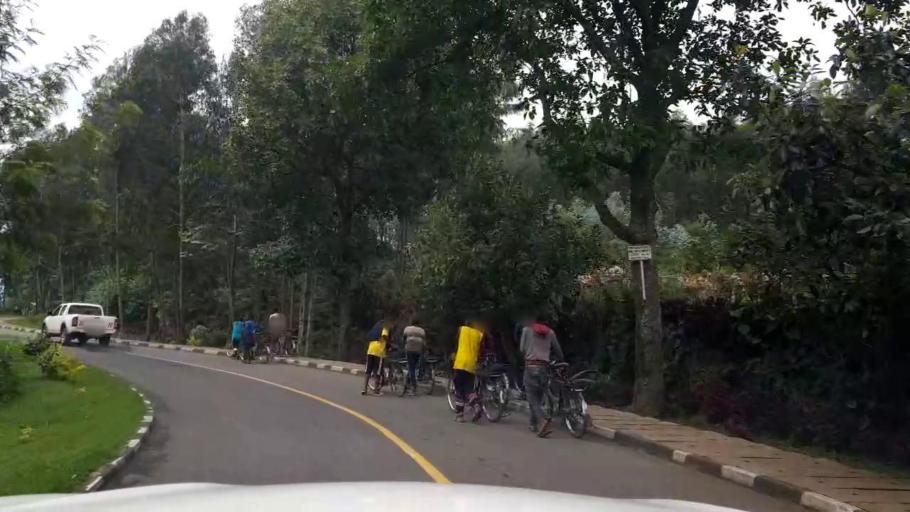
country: RW
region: Northern Province
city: Musanze
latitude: -1.4517
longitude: 29.6052
